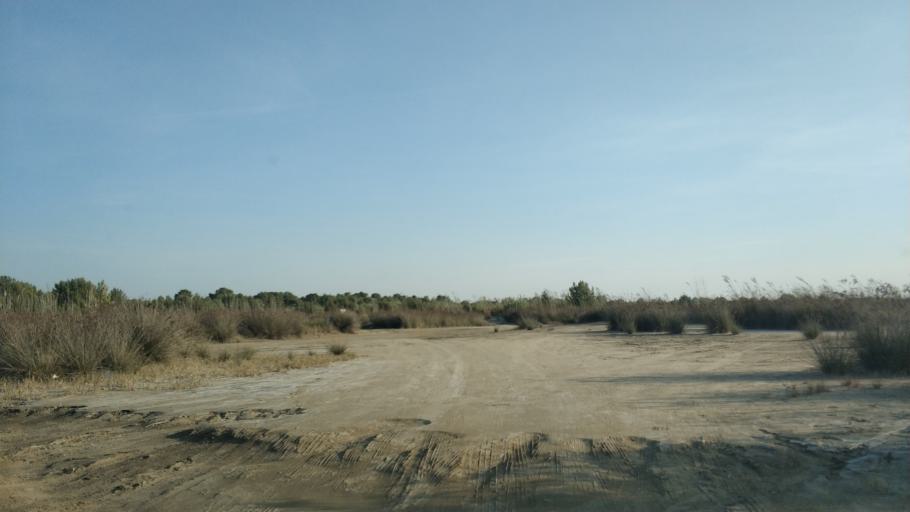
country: AL
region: Fier
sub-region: Rrethi i Lushnjes
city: Divjake
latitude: 40.9563
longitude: 19.4710
